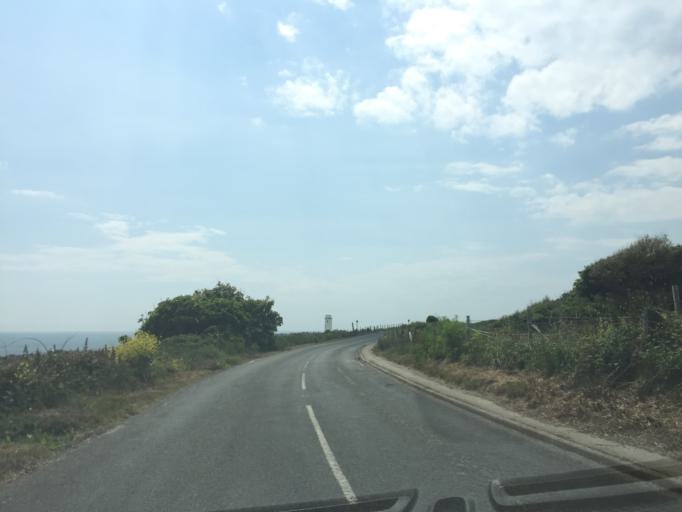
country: GB
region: England
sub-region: Dorset
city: Easton
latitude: 50.5226
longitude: -2.4460
